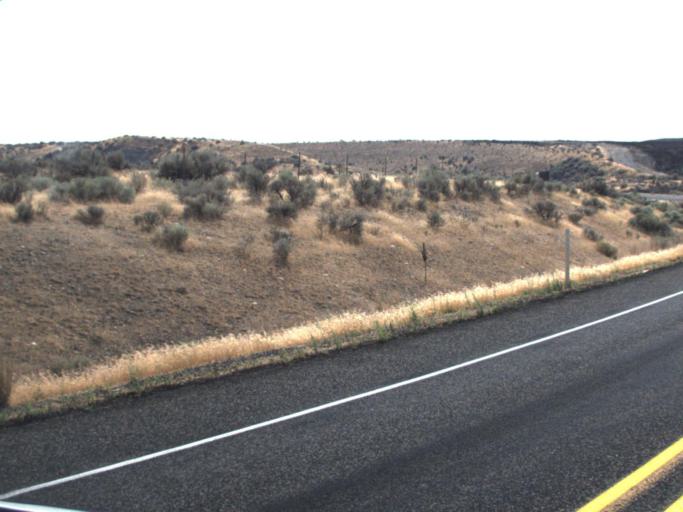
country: US
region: Washington
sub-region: Grant County
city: Desert Aire
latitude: 46.6090
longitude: -119.7366
